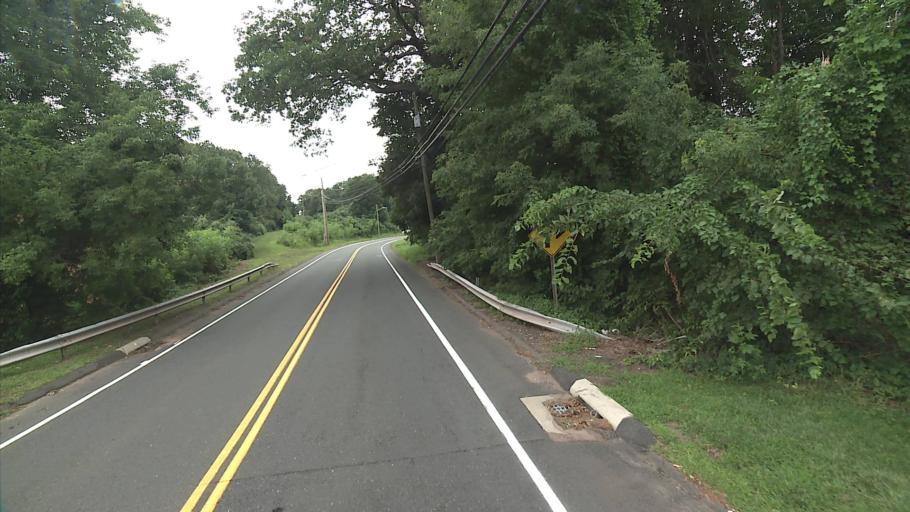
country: US
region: Connecticut
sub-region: Hartford County
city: Manchester
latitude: 41.8319
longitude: -72.5499
